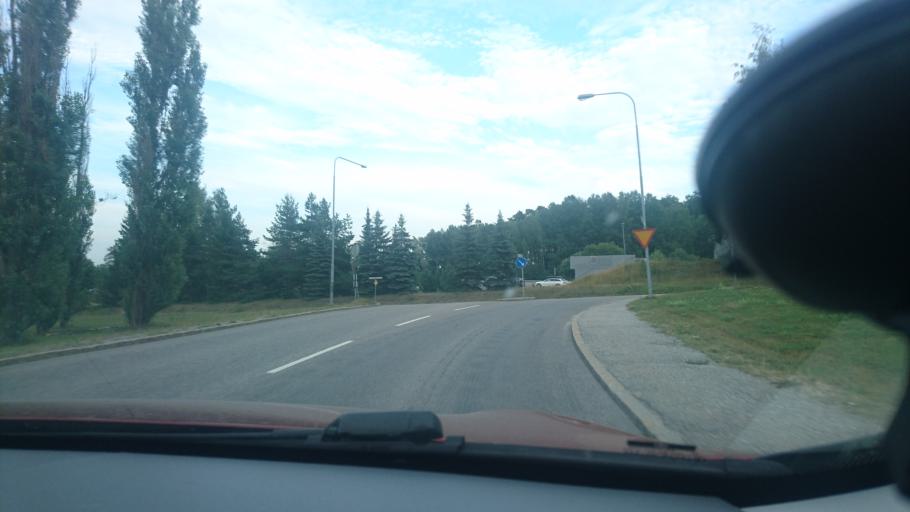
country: SE
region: Stockholm
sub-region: Upplands Vasby Kommun
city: Upplands Vaesby
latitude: 59.5284
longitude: 17.9208
